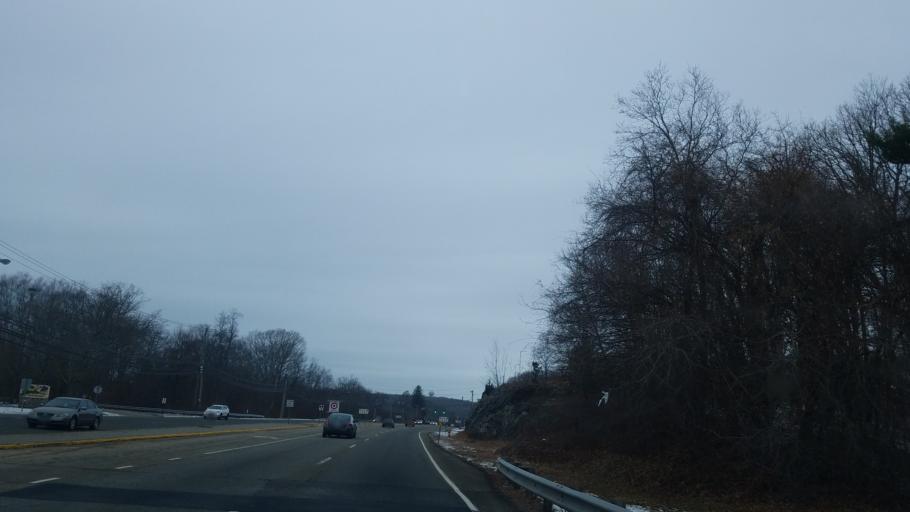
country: US
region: Connecticut
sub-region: New London County
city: Central Waterford
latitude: 41.3776
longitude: -72.1466
